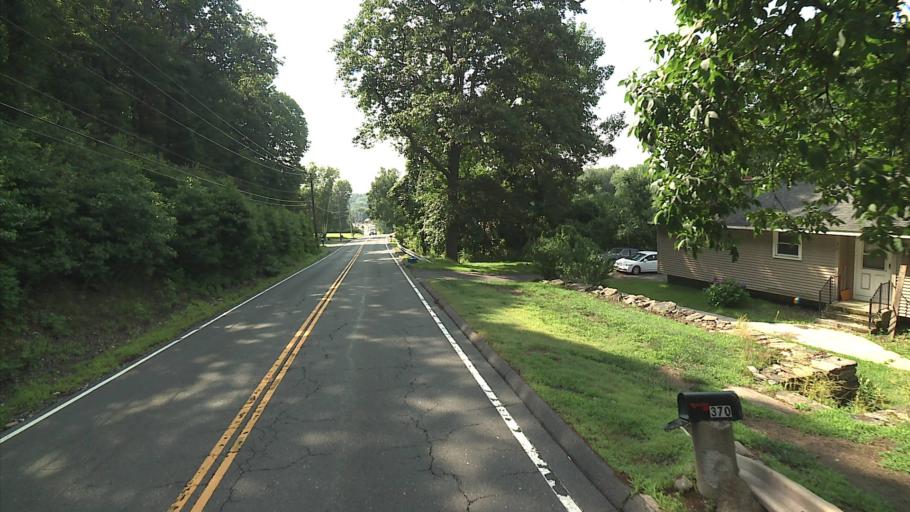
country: US
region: Connecticut
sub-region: New Haven County
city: Wolcott
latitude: 41.6000
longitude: -72.9672
